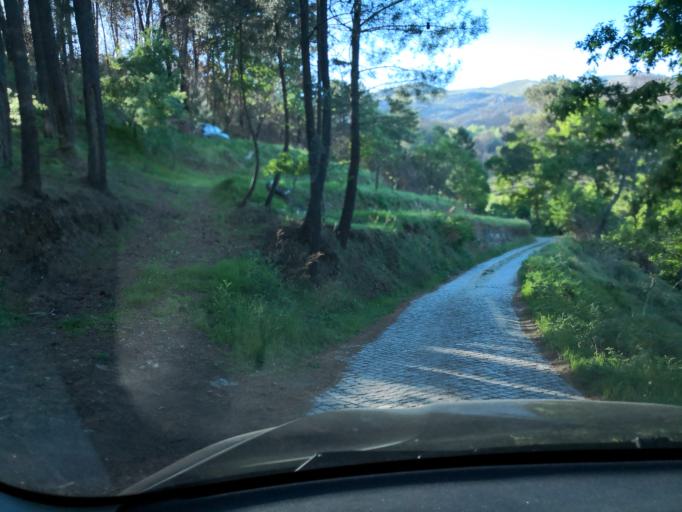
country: PT
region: Vila Real
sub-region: Vila Real
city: Vila Real
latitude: 41.3331
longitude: -7.7534
